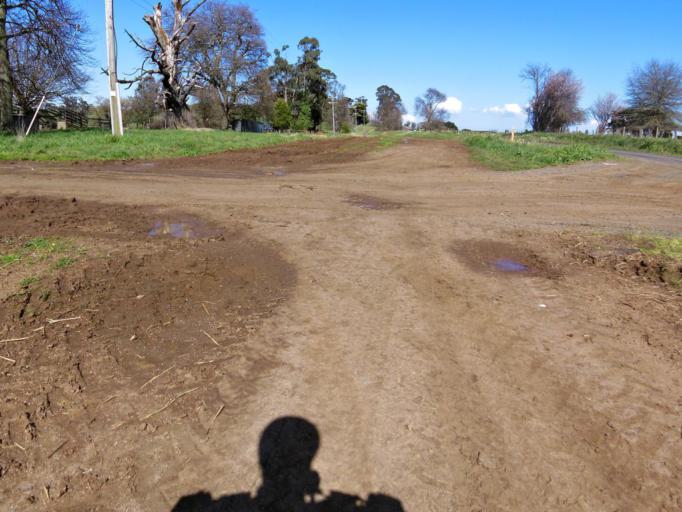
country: AU
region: Victoria
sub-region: Baw Baw
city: Warragul
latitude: -37.9864
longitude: 145.9458
